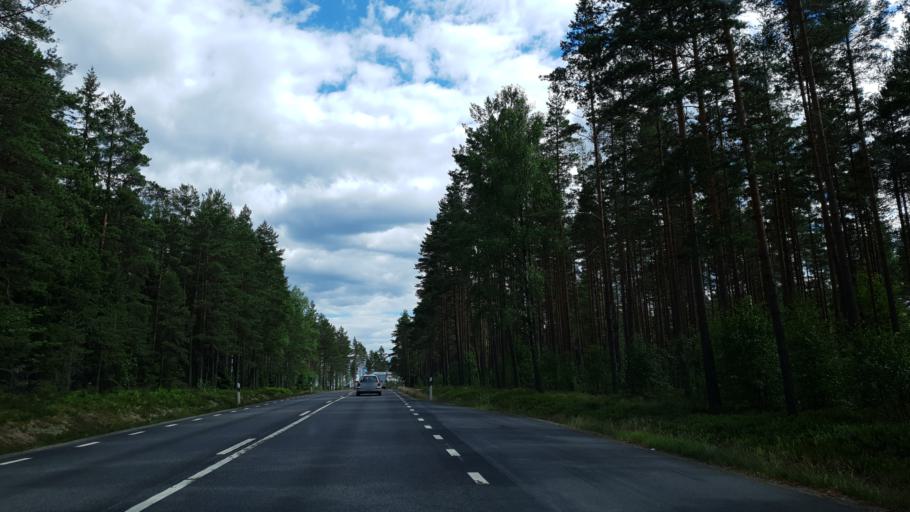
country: SE
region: Kronoberg
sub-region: Lessebo Kommun
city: Lessebo
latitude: 56.8206
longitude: 15.4080
